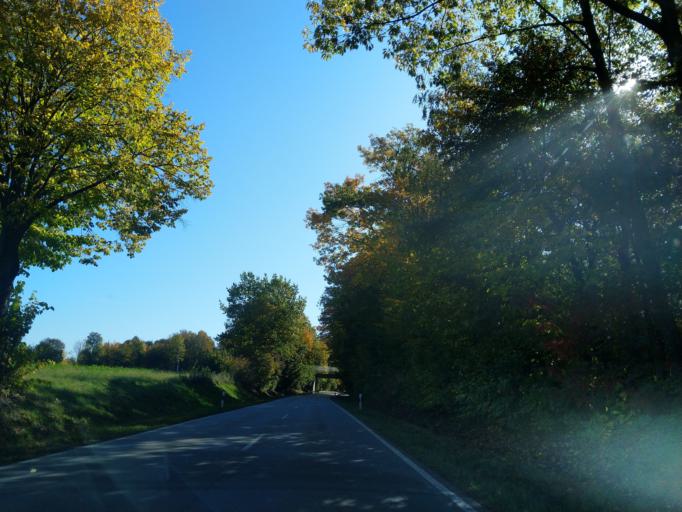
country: DE
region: Bavaria
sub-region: Lower Bavaria
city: Plattling
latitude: 48.8112
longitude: 12.8999
